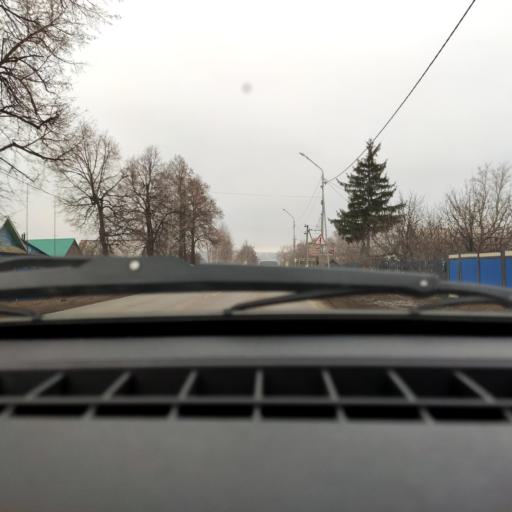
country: RU
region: Bashkortostan
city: Chishmy
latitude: 54.5911
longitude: 55.3926
